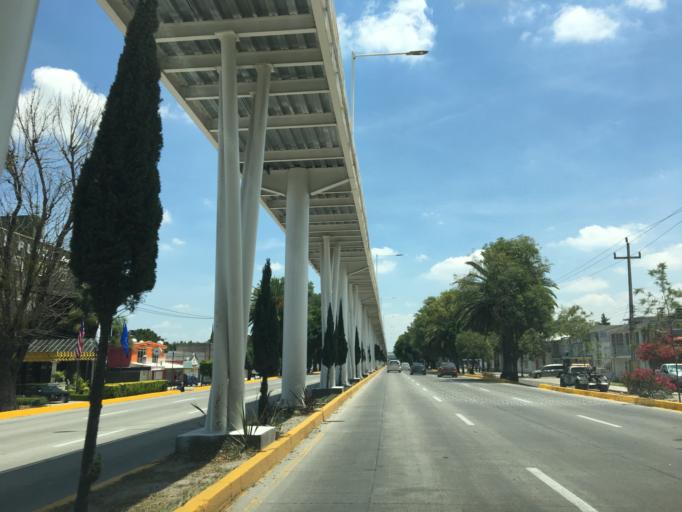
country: MX
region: Puebla
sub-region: Cuautlancingo
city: Sanctorum
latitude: 19.0857
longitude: -98.2289
